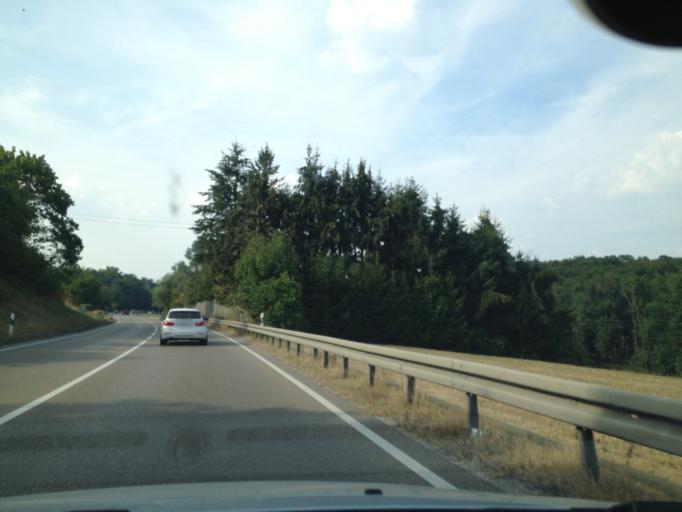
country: DE
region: Bavaria
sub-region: Swabia
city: Donauwoerth
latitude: 48.7429
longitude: 10.7774
